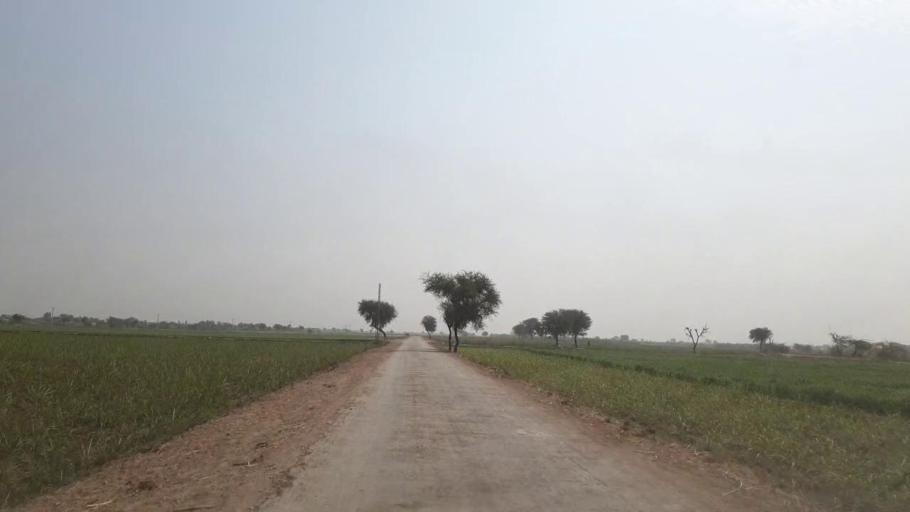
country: PK
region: Sindh
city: Mirpur Khas
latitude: 25.5409
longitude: 69.0863
